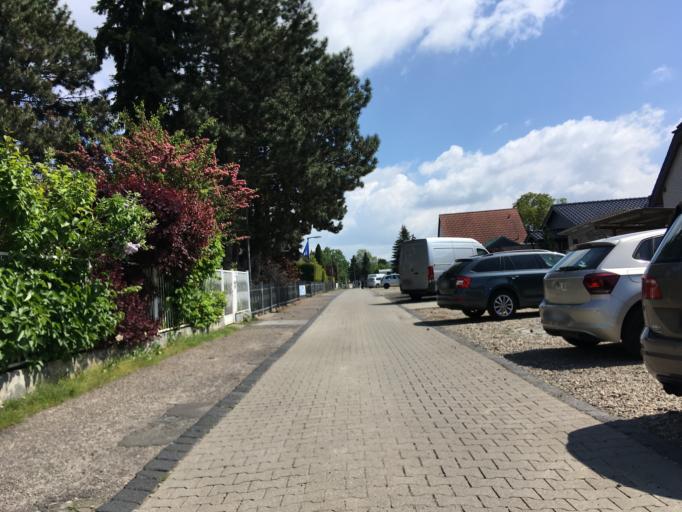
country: DE
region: Berlin
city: Altglienicke
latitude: 52.4131
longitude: 13.5191
